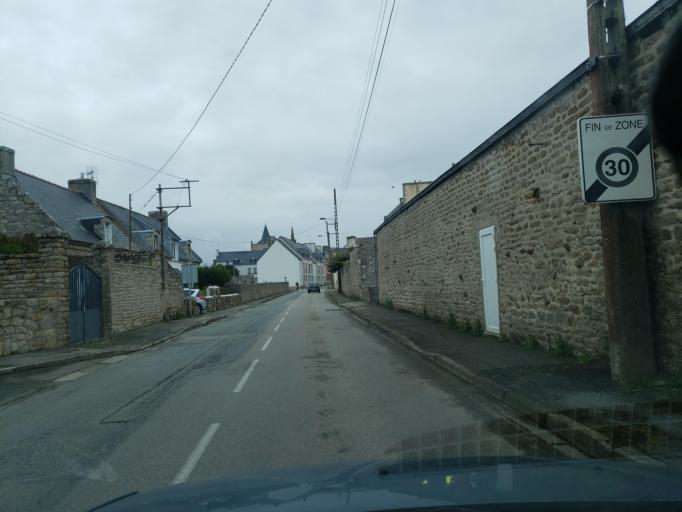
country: FR
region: Brittany
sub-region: Departement du Finistere
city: Guilvinec
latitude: 47.8104
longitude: -4.3412
